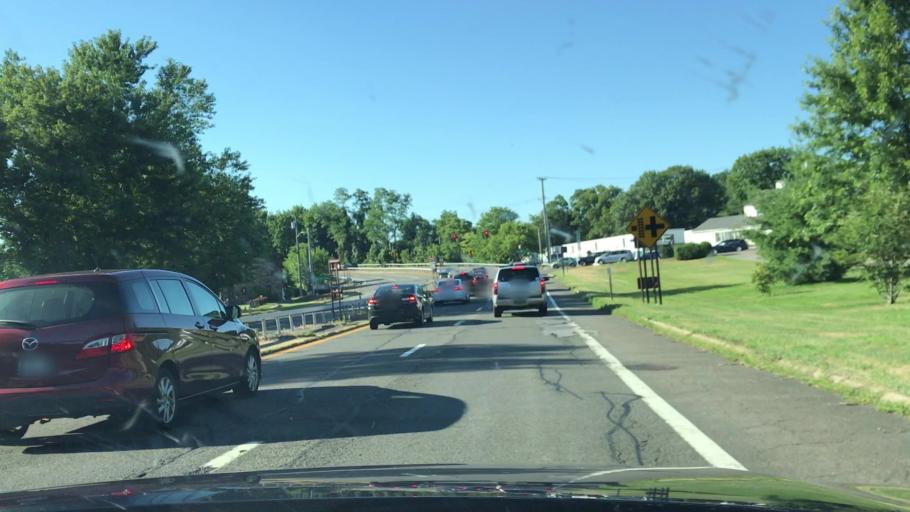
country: US
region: New York
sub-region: Westchester County
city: Hawthorne
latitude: 41.0951
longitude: -73.7930
